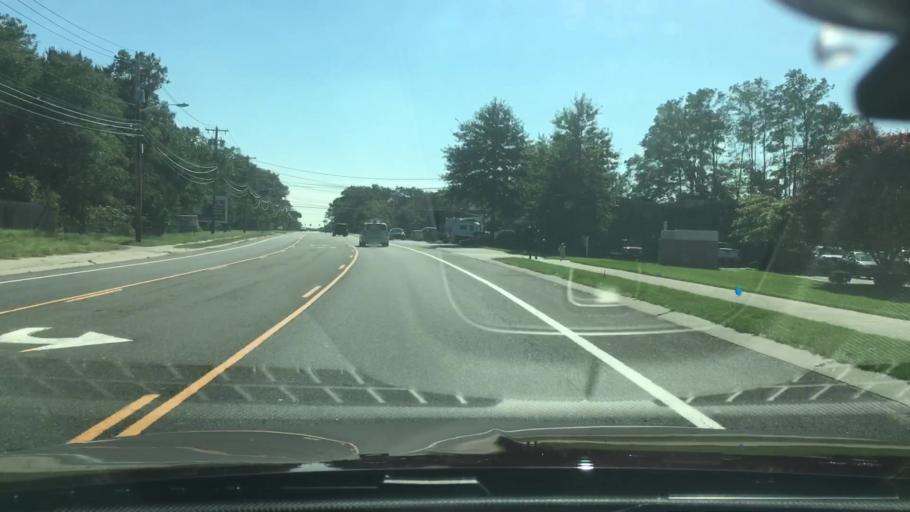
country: US
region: New York
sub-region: Suffolk County
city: Port Jefferson Station
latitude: 40.9056
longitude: -73.0267
